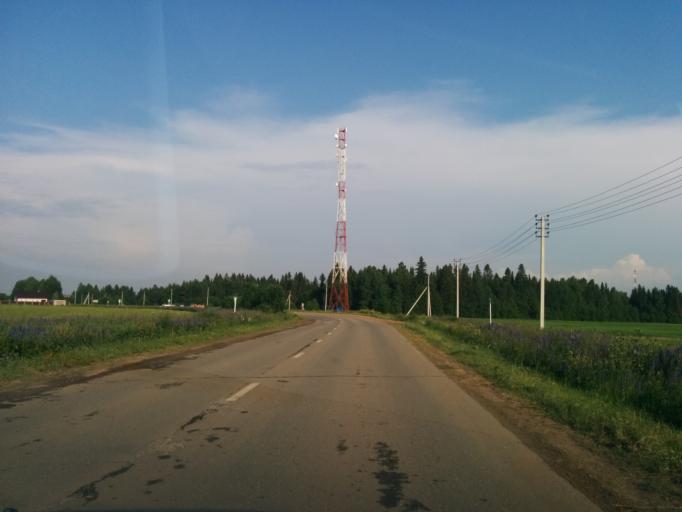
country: RU
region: Perm
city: Polazna
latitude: 58.2380
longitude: 56.2763
